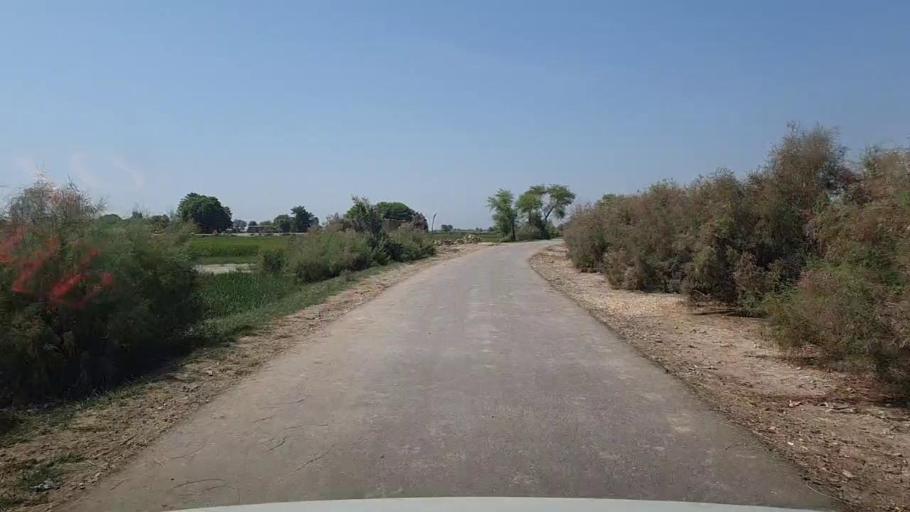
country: PK
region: Sindh
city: Kandhkot
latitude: 28.3221
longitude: 69.3386
